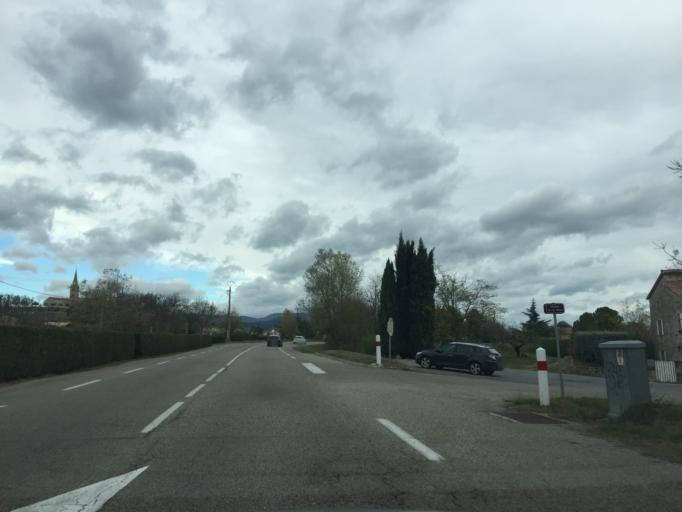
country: FR
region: Rhone-Alpes
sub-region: Departement de l'Ardeche
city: Lablachere
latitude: 44.4562
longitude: 4.2152
